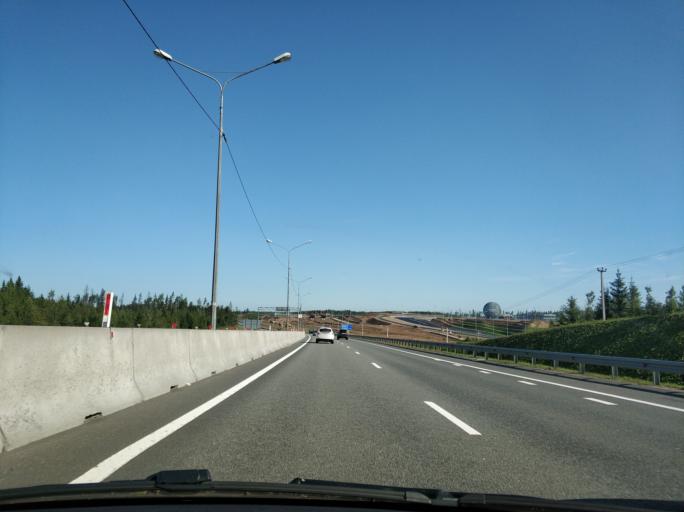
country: RU
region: Leningrad
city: Sosnovo
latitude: 60.5029
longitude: 30.1946
